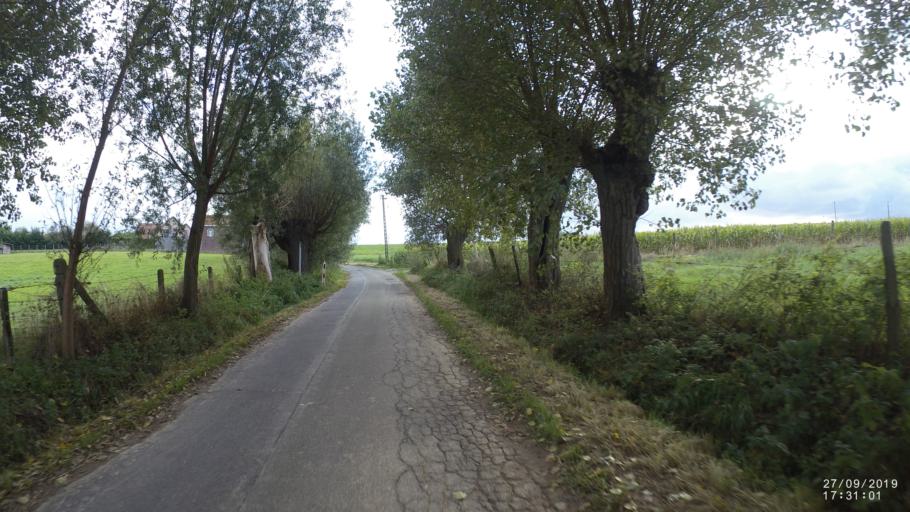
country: BE
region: Flanders
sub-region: Provincie Oost-Vlaanderen
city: Zottegem
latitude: 50.8464
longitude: 3.7867
